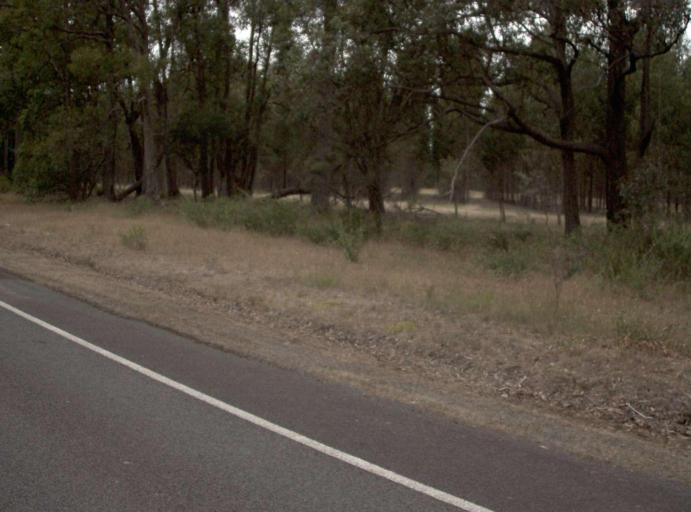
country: AU
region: Victoria
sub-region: Wellington
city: Sale
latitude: -38.4332
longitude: 146.9507
